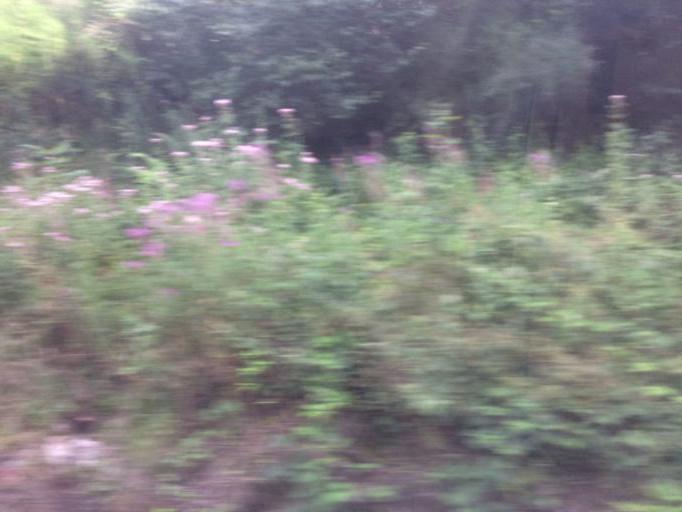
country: GB
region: Scotland
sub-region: Glasgow City
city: Glasgow
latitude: 55.8736
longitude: -4.2439
